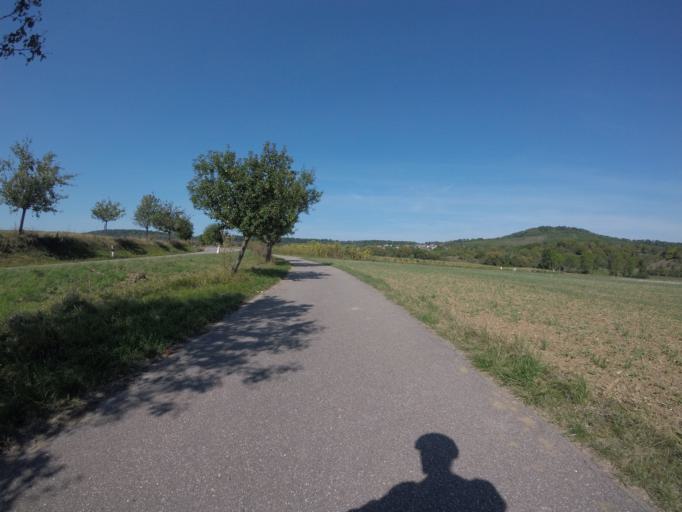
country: DE
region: Baden-Wuerttemberg
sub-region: Regierungsbezirk Stuttgart
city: Grossbottwar
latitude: 49.0161
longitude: 9.2711
